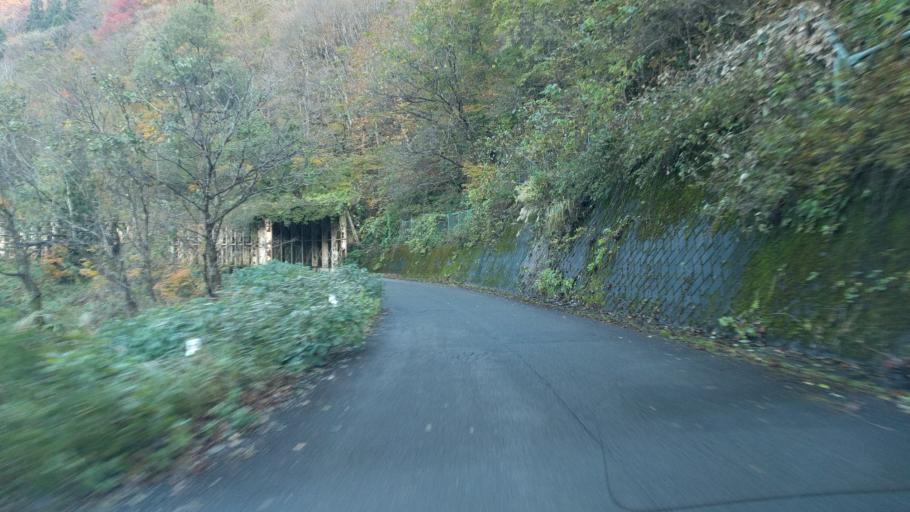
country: JP
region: Fukushima
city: Kitakata
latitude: 37.4535
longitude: 139.6114
